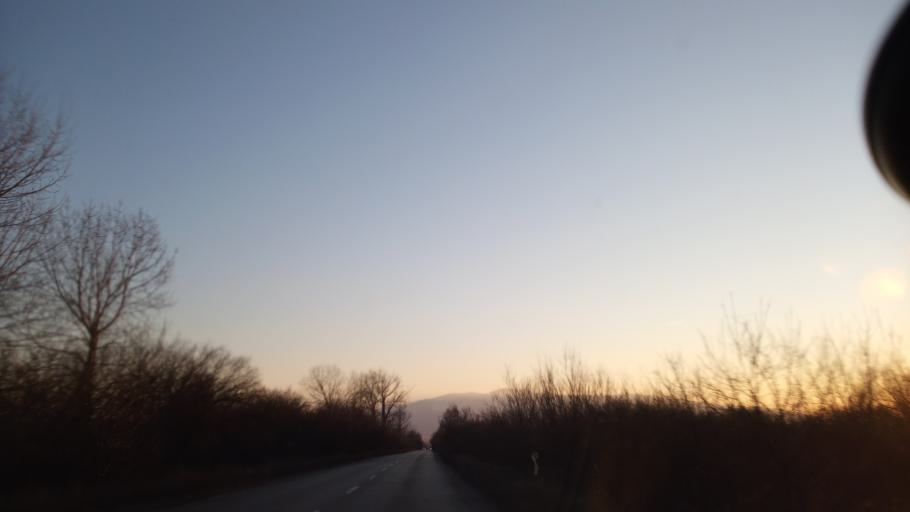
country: BG
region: Sofia-Capital
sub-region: Stolichna Obshtina
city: Bukhovo
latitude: 42.7477
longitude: 23.4777
